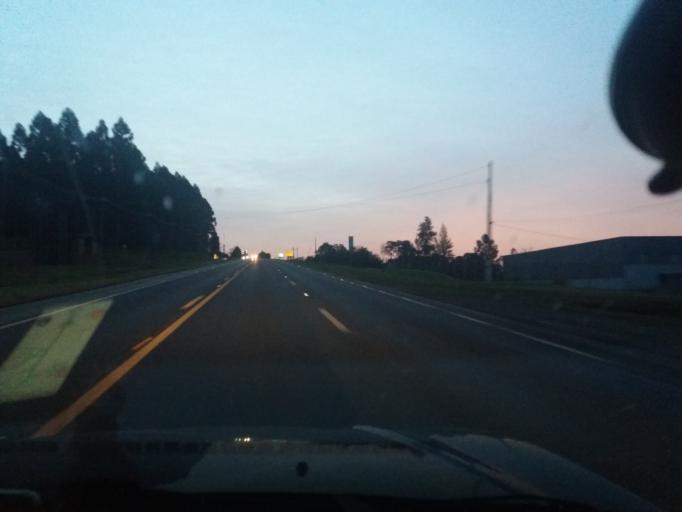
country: BR
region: Sao Paulo
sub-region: Itapeva
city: Itapeva
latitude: -23.9761
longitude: -48.8540
